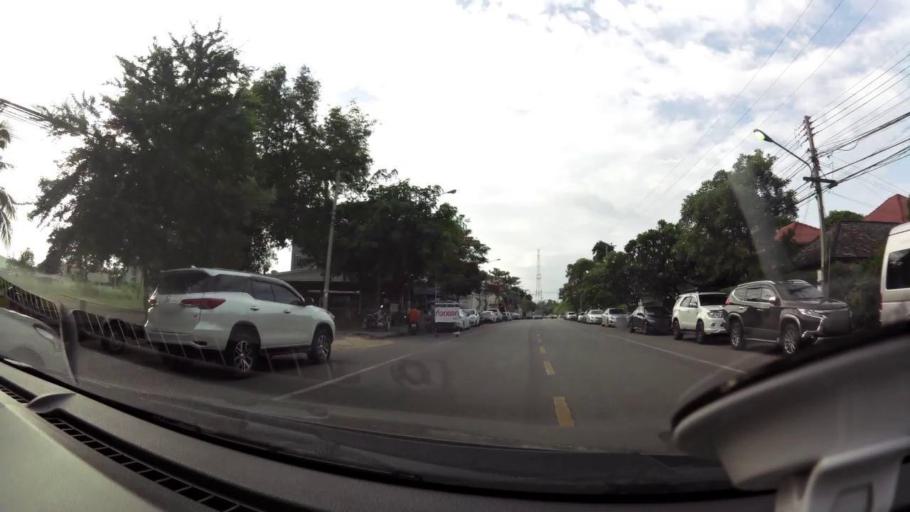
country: TH
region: Prachuap Khiri Khan
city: Hua Hin
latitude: 12.5811
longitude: 99.9557
